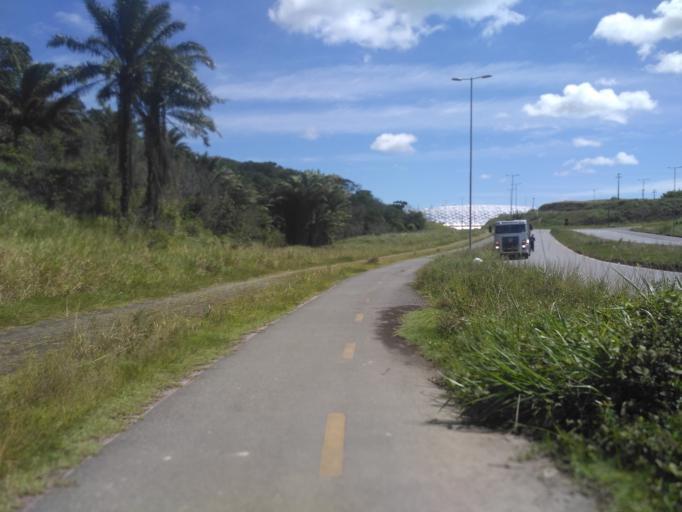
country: BR
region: Pernambuco
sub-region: Sao Lourenco Da Mata
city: Sao Lourenco da Mata
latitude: -8.0445
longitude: -35.0037
